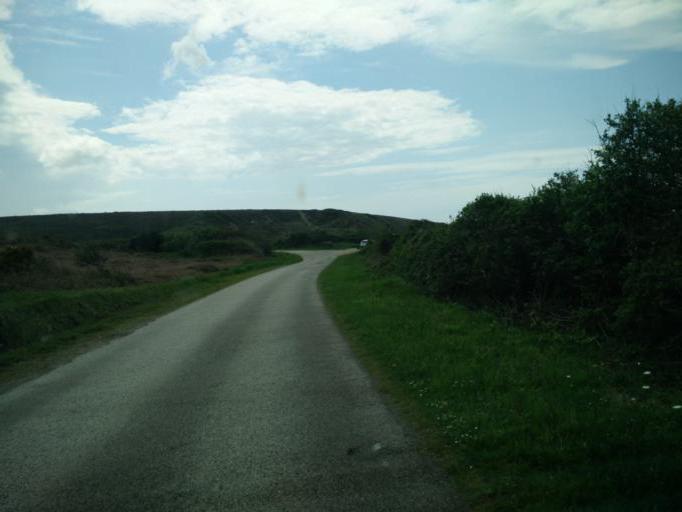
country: FR
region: Brittany
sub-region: Departement du Finistere
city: Roscanvel
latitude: 48.3080
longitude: -4.5699
